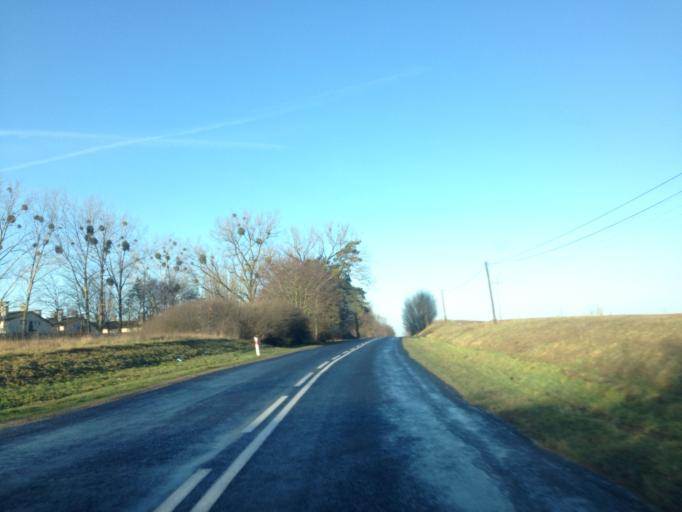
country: PL
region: Kujawsko-Pomorskie
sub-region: Powiat brodnicki
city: Bobrowo
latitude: 53.3321
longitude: 19.2314
